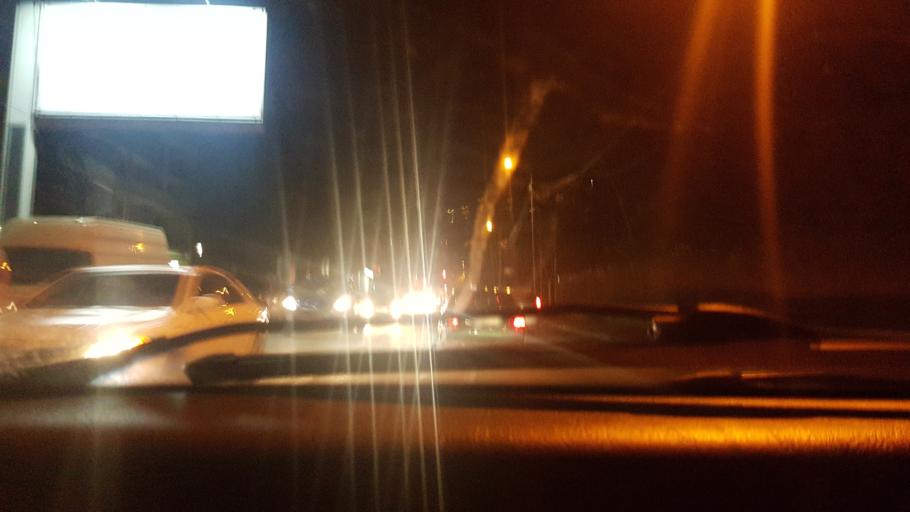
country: GE
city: Tsqnet'i
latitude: 41.7228
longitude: 44.7508
